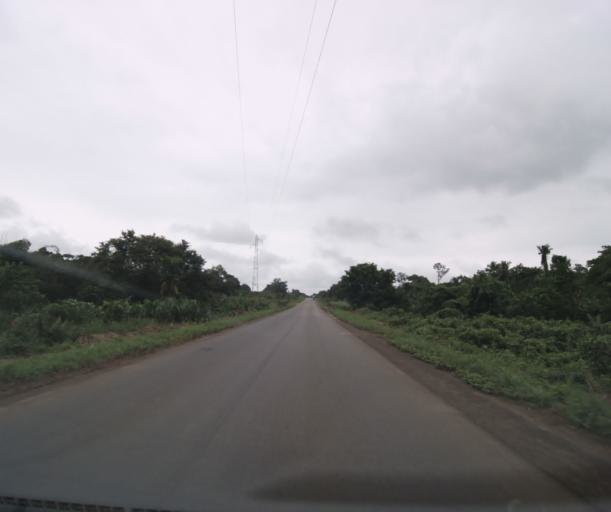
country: CM
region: Littoral
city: Edea
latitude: 3.7311
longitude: 10.1132
